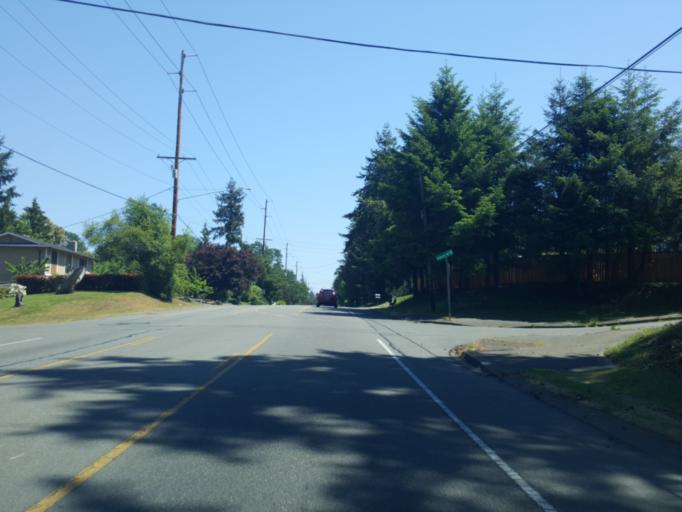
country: US
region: Washington
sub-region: Pierce County
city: Lakewood
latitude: 47.1485
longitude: -122.5560
